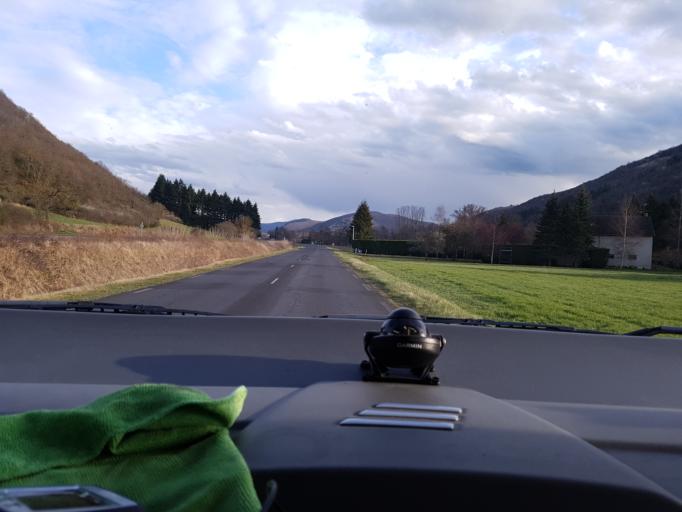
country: FR
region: Auvergne
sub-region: Departement du Cantal
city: Massiac
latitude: 45.2732
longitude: 3.1928
